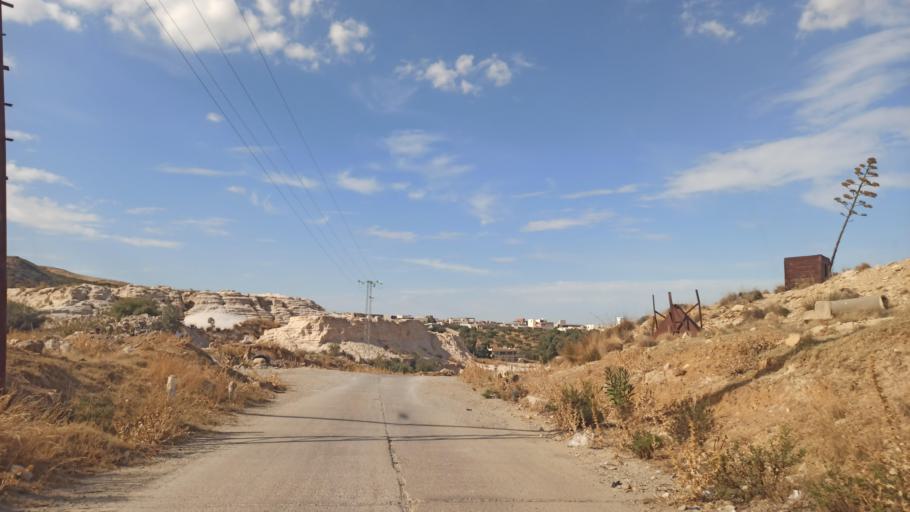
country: TN
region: Zaghwan
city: Zaghouan
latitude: 36.3419
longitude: 10.2081
